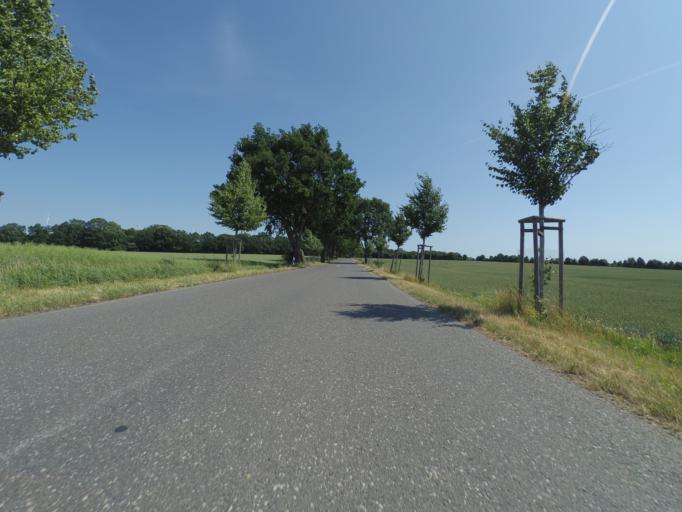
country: DE
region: Brandenburg
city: Heiligengrabe
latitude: 53.1635
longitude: 12.2802
